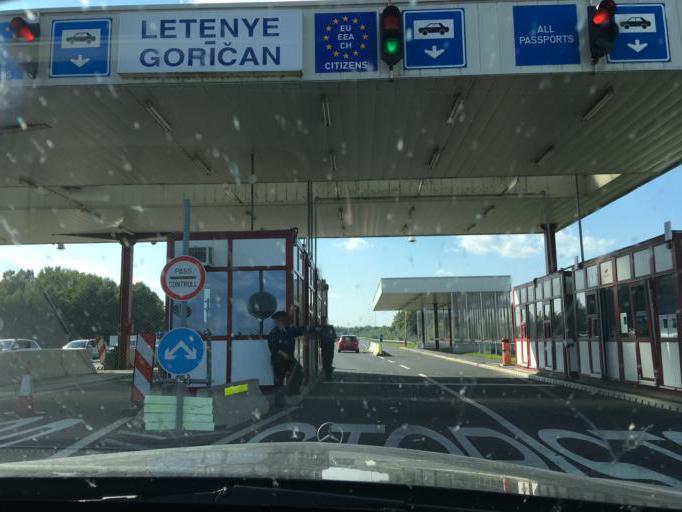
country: HU
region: Zala
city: Letenye
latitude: 46.4124
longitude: 16.7133
